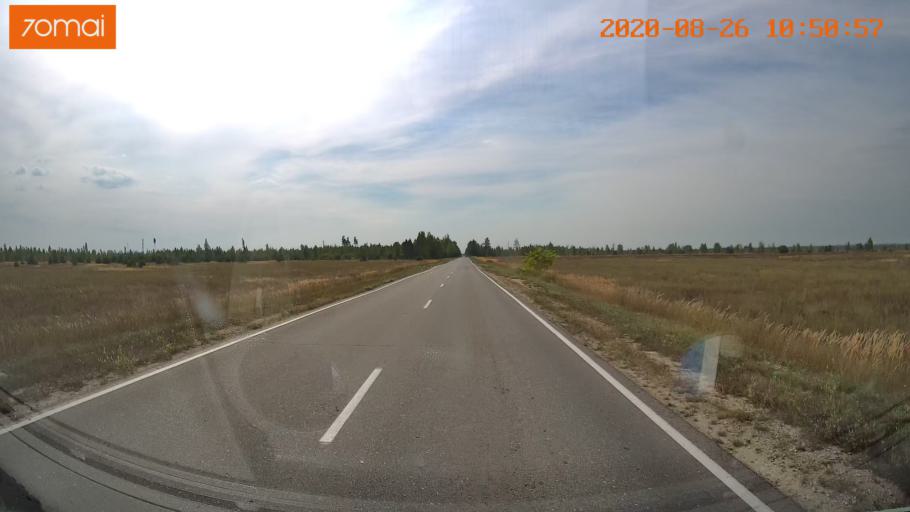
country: RU
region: Rjazan
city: Lashma
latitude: 54.6797
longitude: 41.1559
